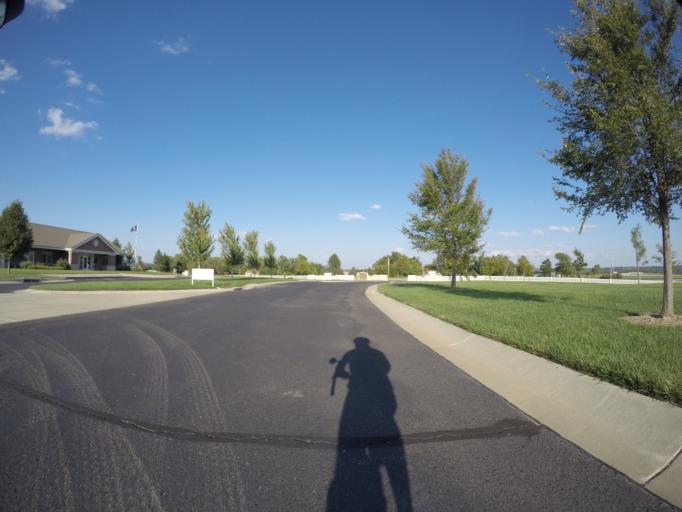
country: US
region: Kansas
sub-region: Riley County
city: Ogden
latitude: 39.1361
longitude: -96.6836
